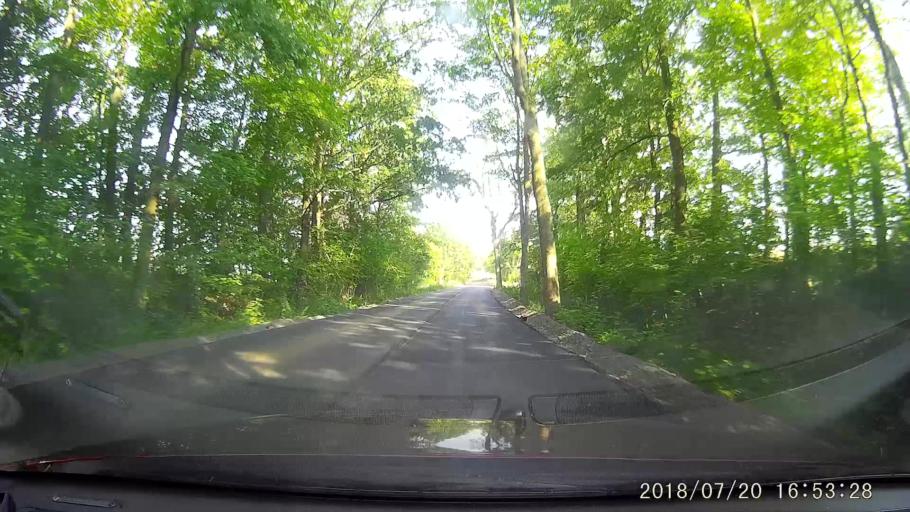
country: PL
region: Lower Silesian Voivodeship
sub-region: Powiat lubanski
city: Lesna
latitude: 51.0363
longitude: 15.2415
